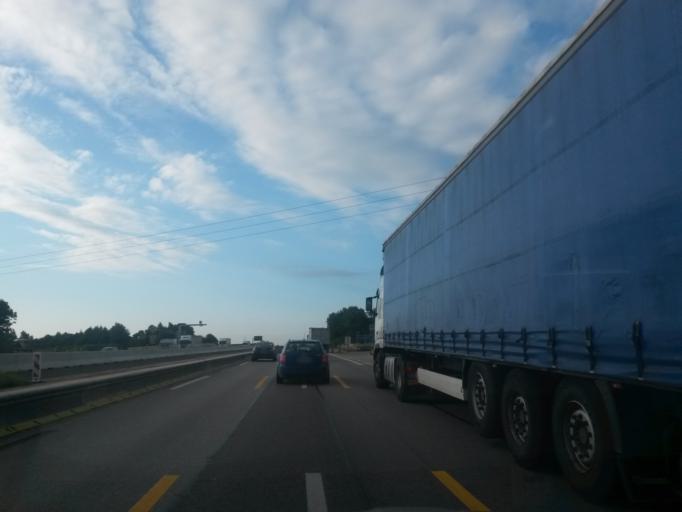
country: DE
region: Bavaria
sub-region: Upper Bavaria
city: Schweitenkirchen
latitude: 48.5070
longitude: 11.5872
